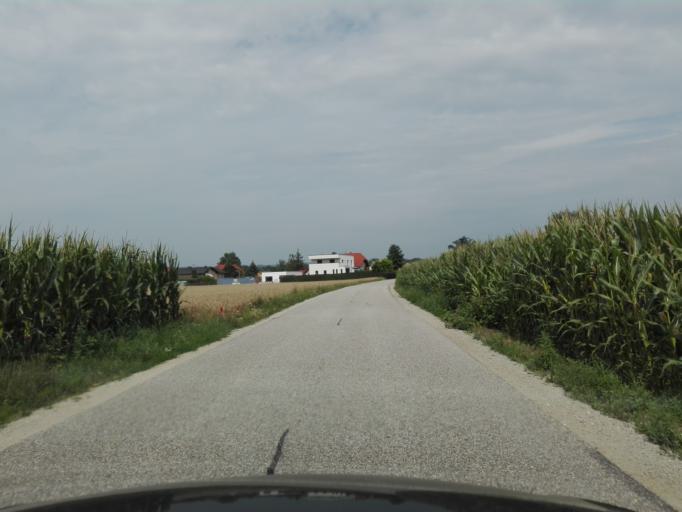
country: AT
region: Lower Austria
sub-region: Politischer Bezirk Amstetten
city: Strengberg
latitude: 48.1860
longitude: 14.6887
